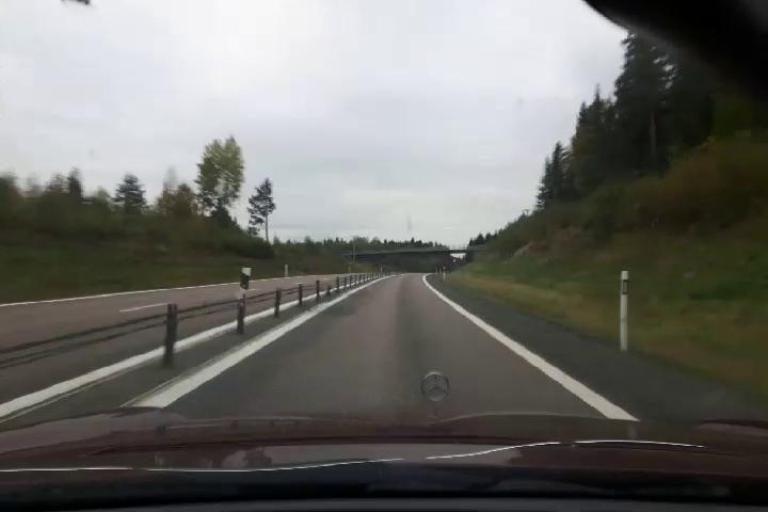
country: SE
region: Vaesternorrland
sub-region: Kramfors Kommun
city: Nordingra
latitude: 62.9162
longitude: 18.0961
